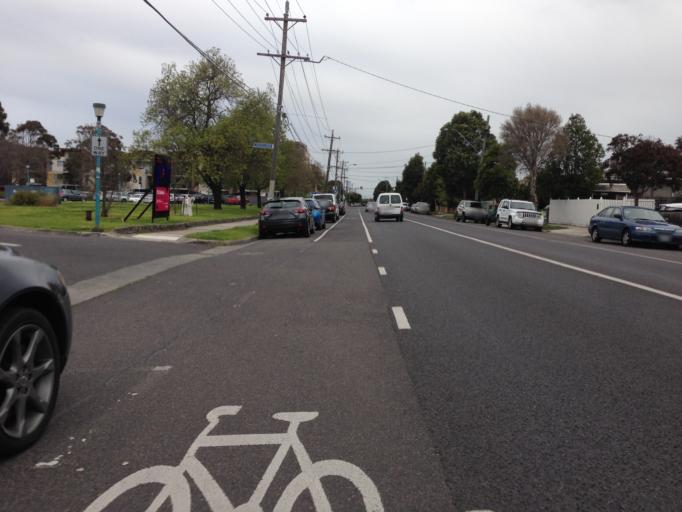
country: AU
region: Victoria
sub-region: Darebin
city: Northcote
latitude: -37.7686
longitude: 145.0117
